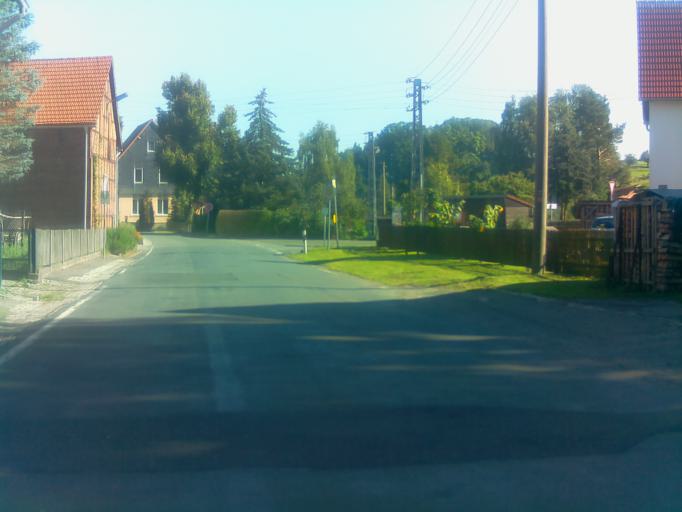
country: DE
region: Thuringia
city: Trockenborn-Wolfersdorf
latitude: 50.7885
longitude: 11.6918
